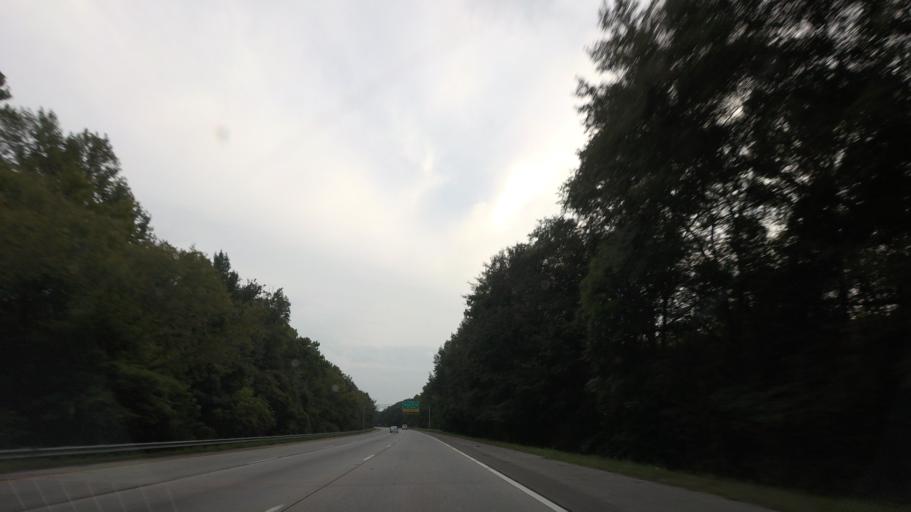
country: US
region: Georgia
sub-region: Bibb County
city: Macon
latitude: 32.7673
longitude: -83.7005
